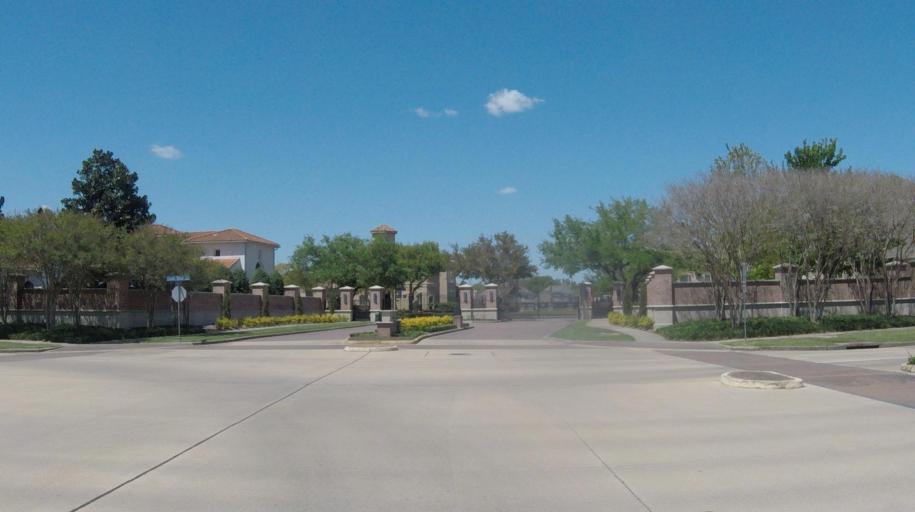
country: US
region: Texas
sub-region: Fort Bend County
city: Sugar Land
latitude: 29.6073
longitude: -95.6215
